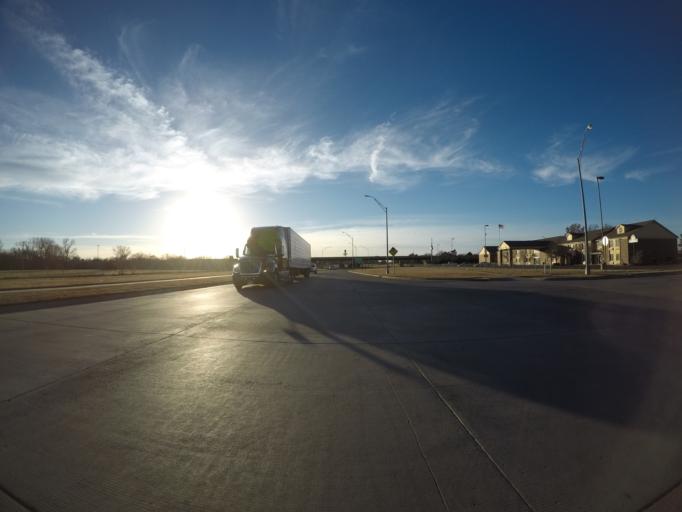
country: US
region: Kansas
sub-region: Harvey County
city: Newton
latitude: 38.0427
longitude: -97.3203
